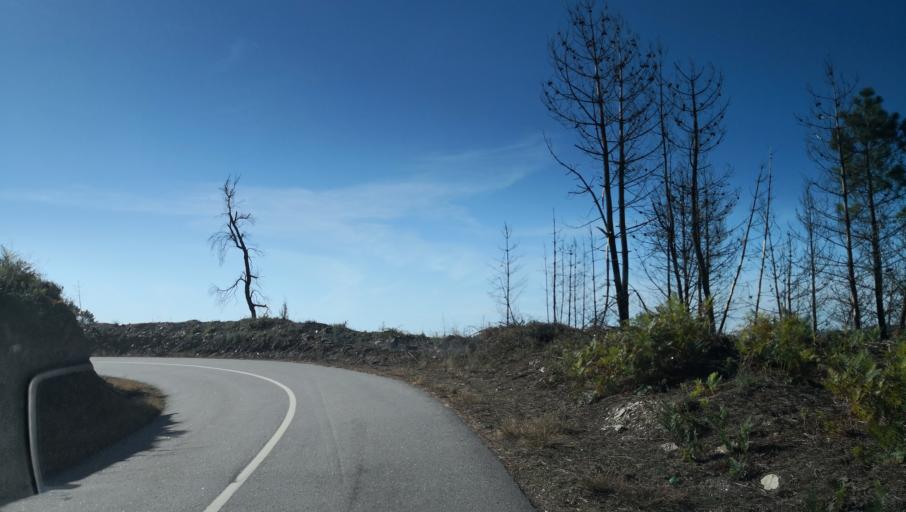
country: PT
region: Vila Real
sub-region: Sabrosa
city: Vilela
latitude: 41.2362
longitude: -7.6406
